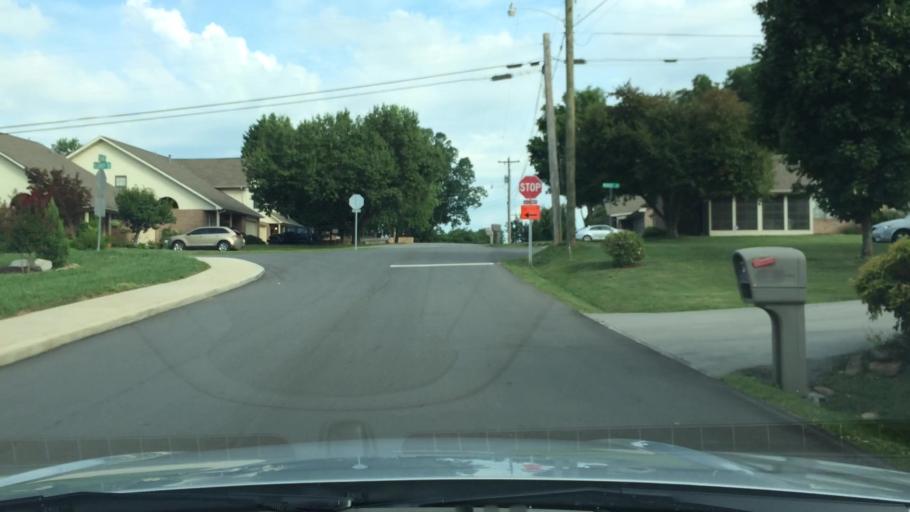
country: US
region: Tennessee
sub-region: Blount County
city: Eagleton Village
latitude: 35.7619
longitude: -83.9318
